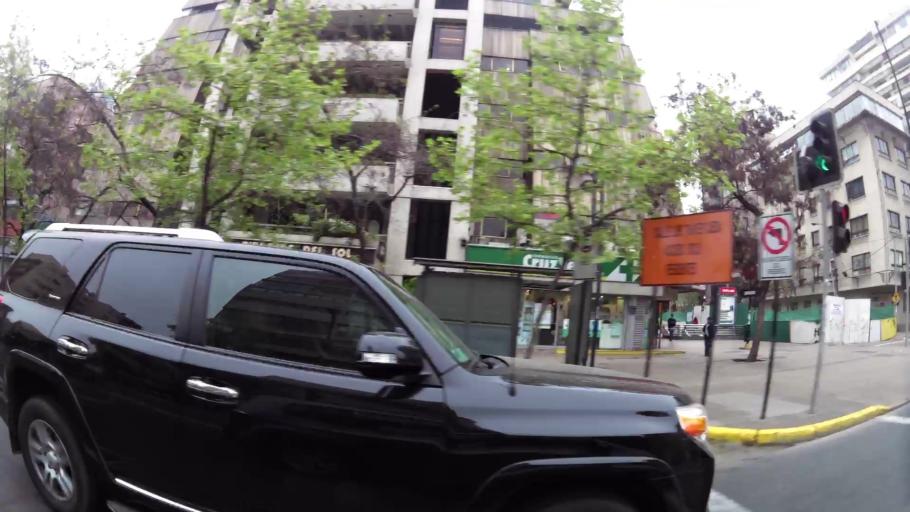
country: CL
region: Santiago Metropolitan
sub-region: Provincia de Santiago
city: Villa Presidente Frei, Nunoa, Santiago, Chile
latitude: -33.4187
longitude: -70.6028
